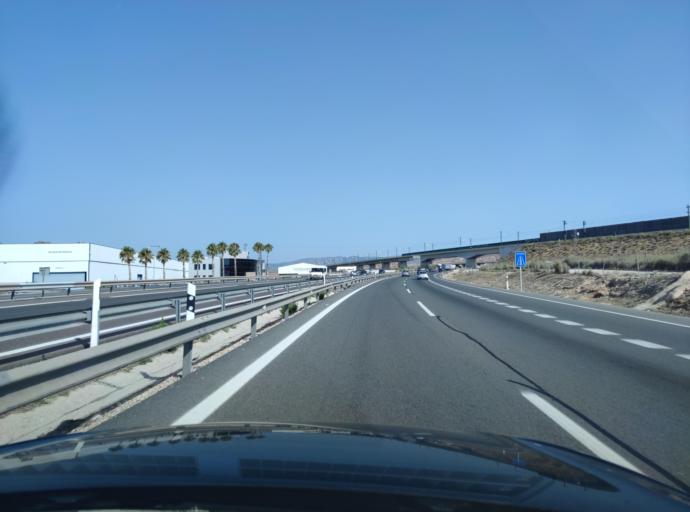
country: ES
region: Valencia
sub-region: Provincia de Alicante
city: Novelda
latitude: 38.4084
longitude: -0.7764
